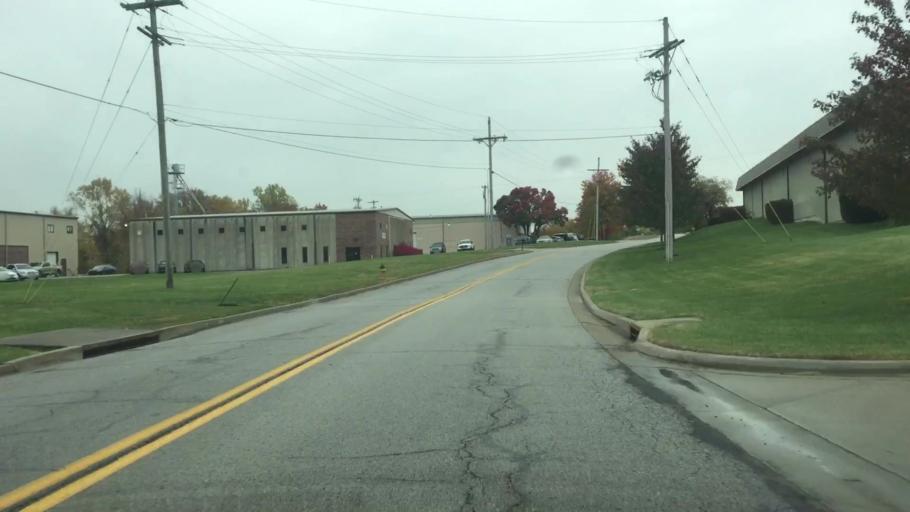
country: US
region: Kansas
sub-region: Wyandotte County
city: Edwardsville
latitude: 39.0057
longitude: -94.8236
